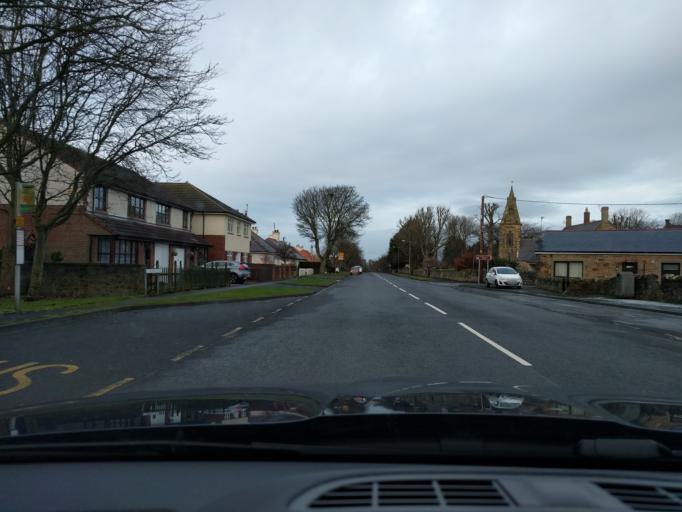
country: GB
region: England
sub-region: Northumberland
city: Ancroft
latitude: 55.7360
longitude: -1.9908
